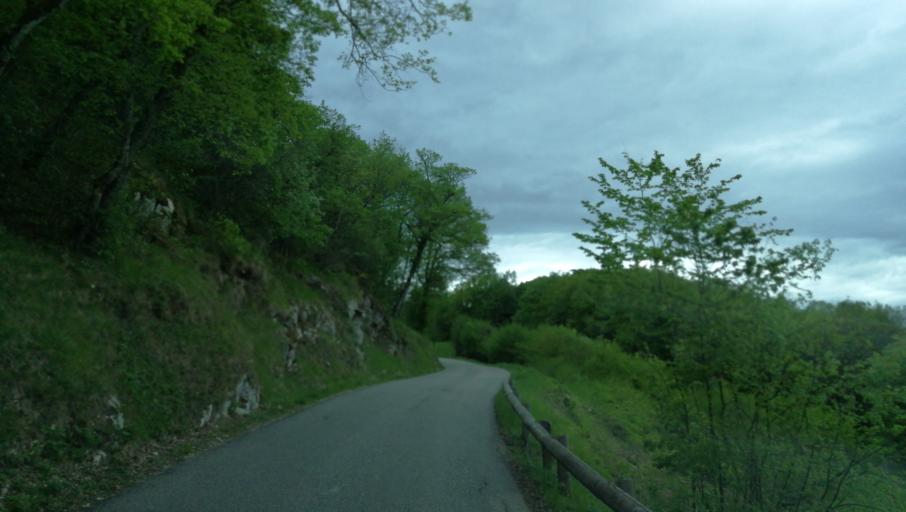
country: FR
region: Rhone-Alpes
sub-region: Departement de la Savoie
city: Chatillon
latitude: 45.7849
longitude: 5.8208
